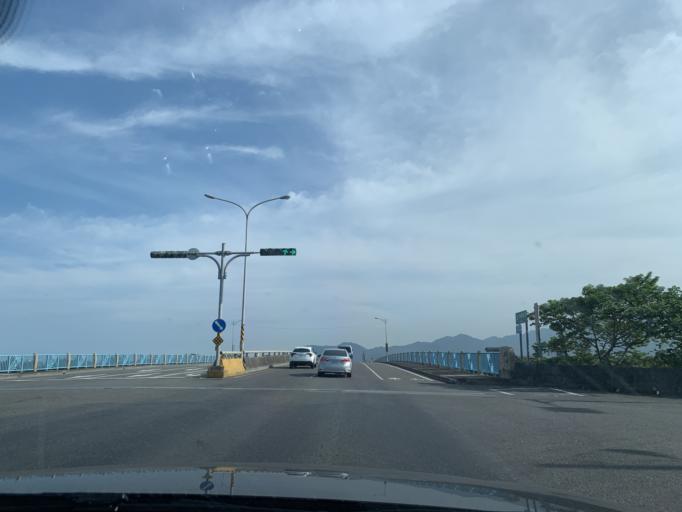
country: TW
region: Taiwan
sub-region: Yilan
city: Yilan
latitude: 24.6925
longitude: 121.8249
